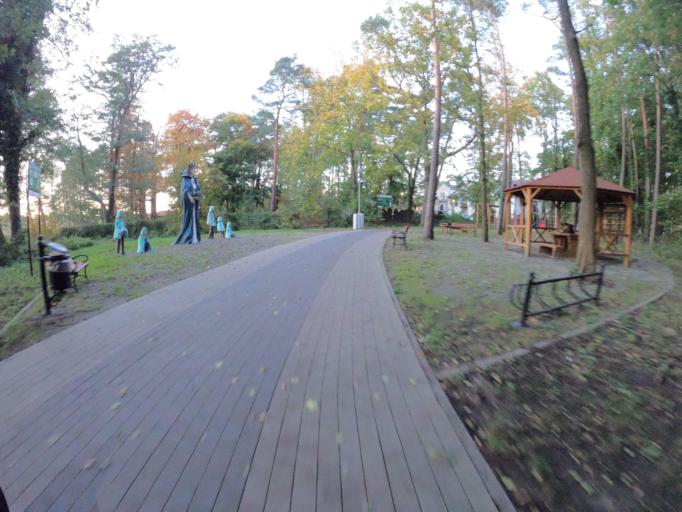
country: PL
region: West Pomeranian Voivodeship
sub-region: Powiat mysliborski
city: Barlinek
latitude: 52.9874
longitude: 15.2254
